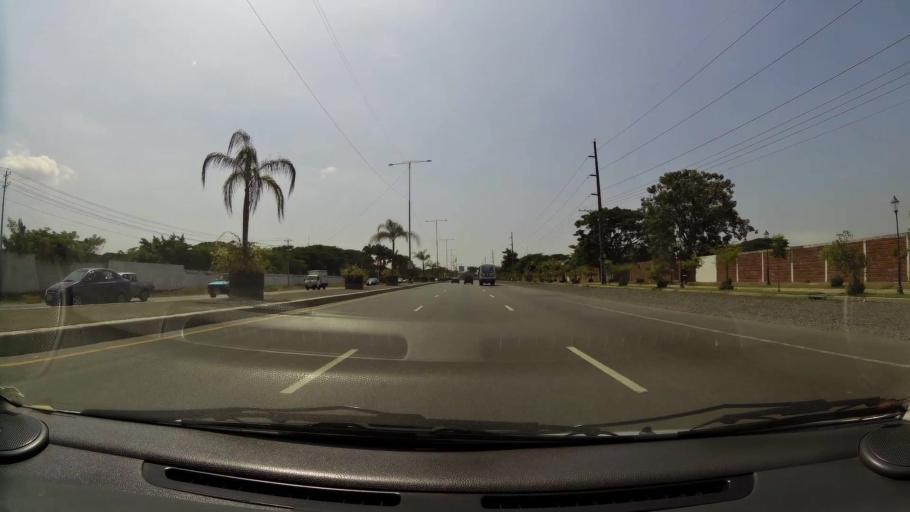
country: EC
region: Guayas
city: Eloy Alfaro
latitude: -2.0664
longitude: -79.8727
